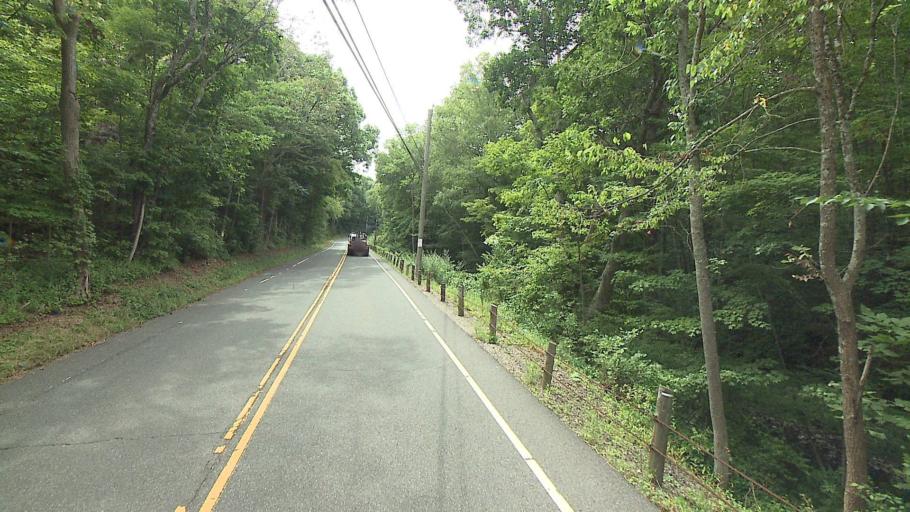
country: US
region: Connecticut
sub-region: Litchfield County
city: Woodbury
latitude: 41.5930
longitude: -73.2565
